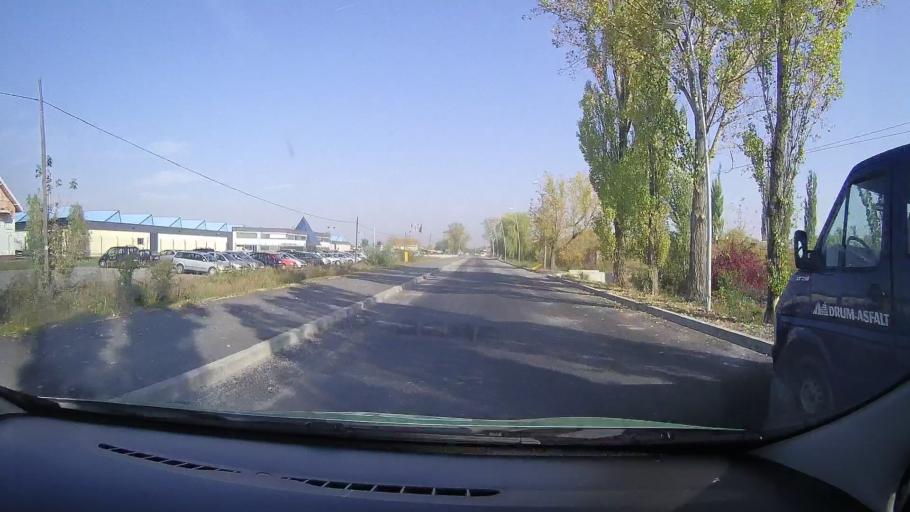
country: RO
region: Bihor
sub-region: Municipiul Salonta
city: Salonta
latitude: 46.7903
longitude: 21.6637
